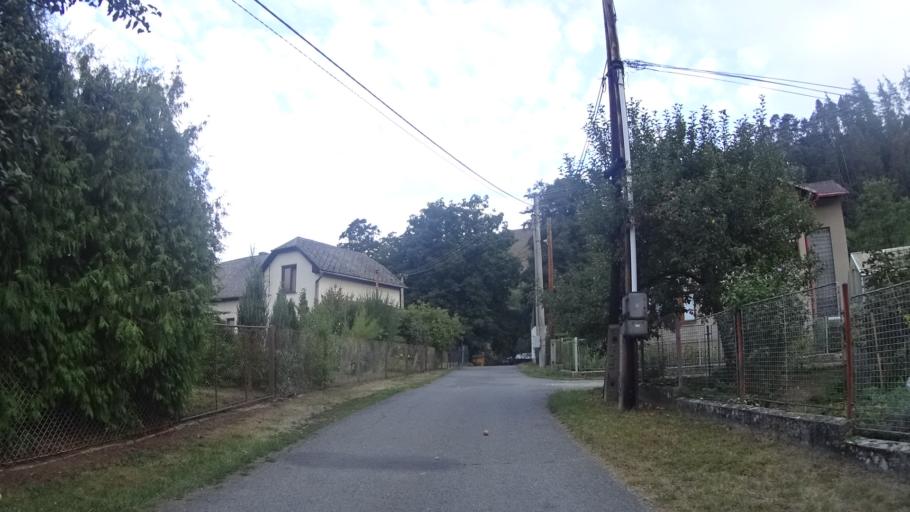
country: CZ
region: Olomoucky
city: Stity
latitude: 49.8752
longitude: 16.7796
